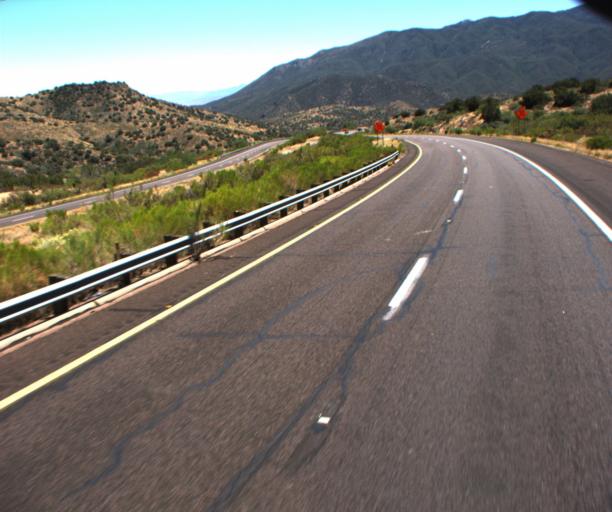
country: US
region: Arizona
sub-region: Gila County
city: Tonto Basin
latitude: 33.9886
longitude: -111.3835
